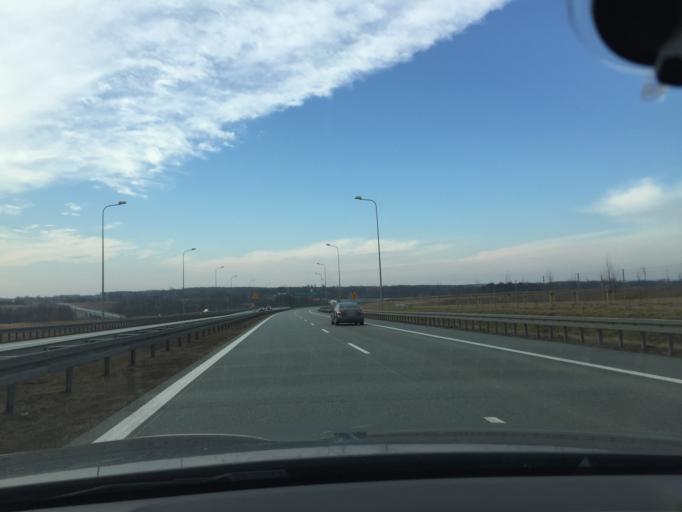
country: PL
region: Lodz Voivodeship
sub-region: Powiat skierniewicki
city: Kowiesy
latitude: 51.8469
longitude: 20.3651
